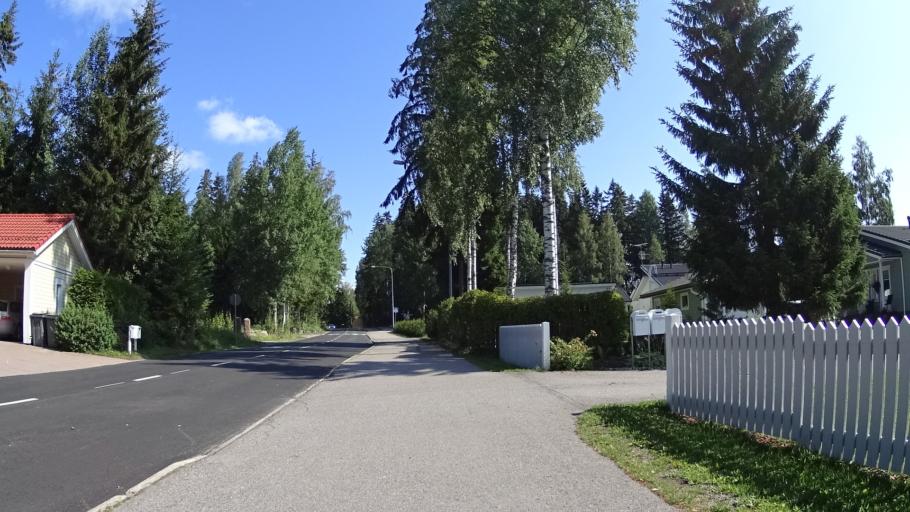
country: FI
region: Uusimaa
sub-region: Helsinki
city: Tuusula
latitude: 60.4079
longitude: 25.0282
